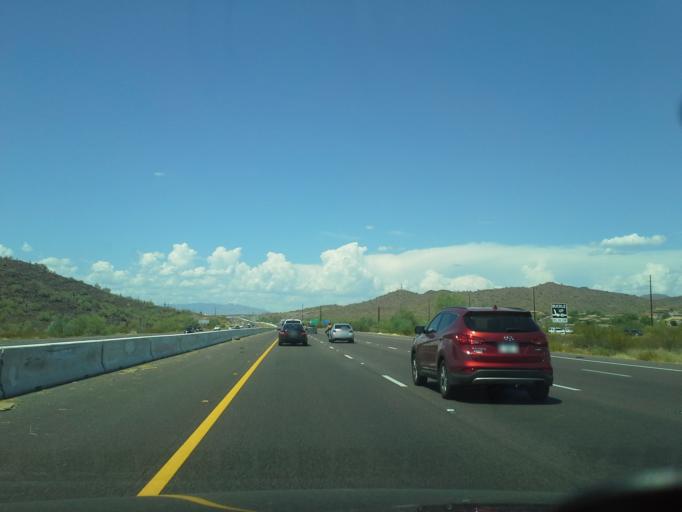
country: US
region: Arizona
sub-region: Maricopa County
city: Anthem
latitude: 33.8047
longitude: -112.1367
